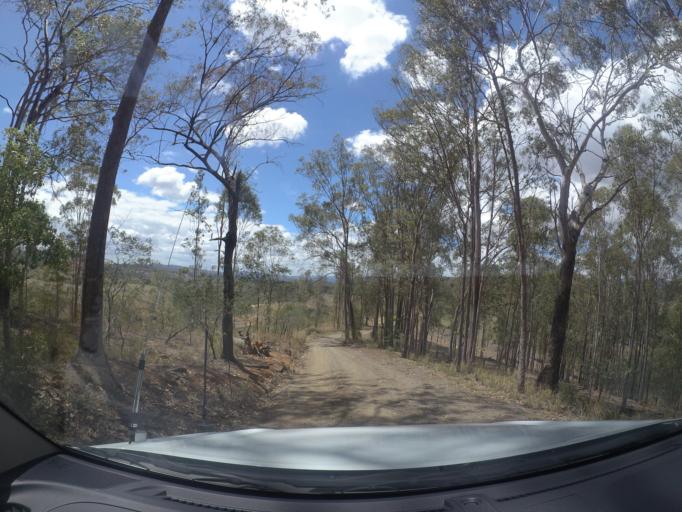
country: AU
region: Queensland
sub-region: Logan
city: Cedar Vale
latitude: -27.9162
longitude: 153.0486
